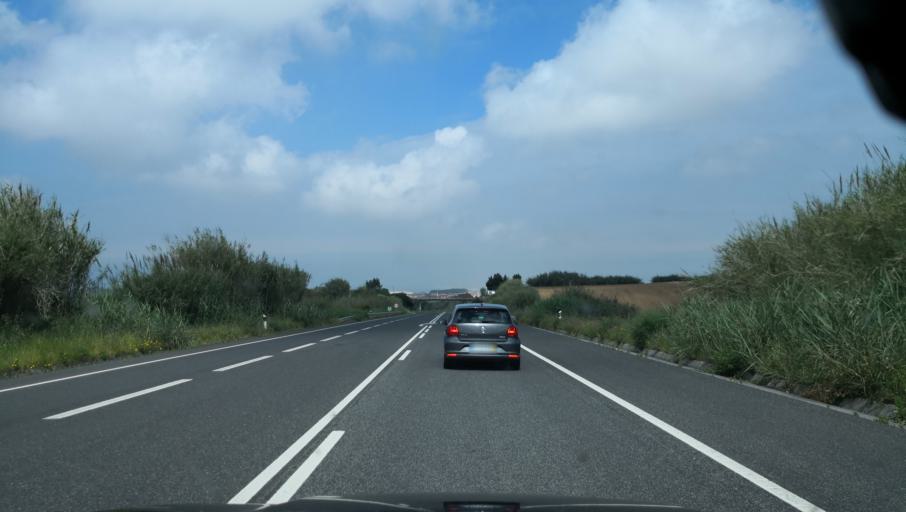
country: PT
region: Leiria
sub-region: Peniche
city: Atouguia da Baleia
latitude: 39.3252
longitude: -9.2818
